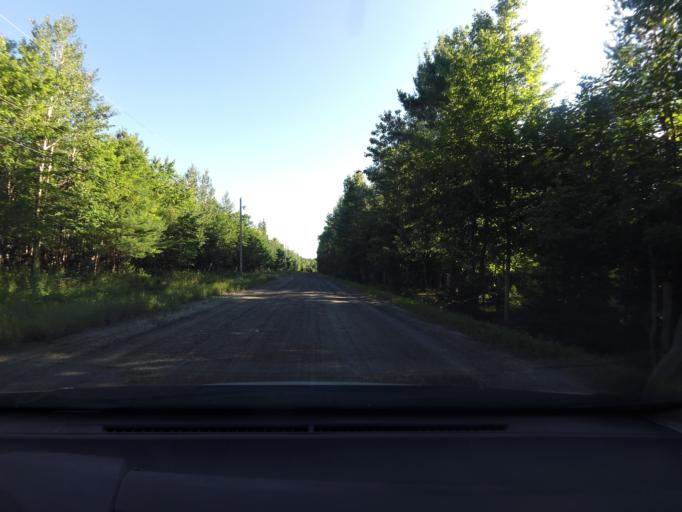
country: CA
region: Quebec
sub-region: Mauricie
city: Becancour
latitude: 46.5467
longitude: -72.3956
